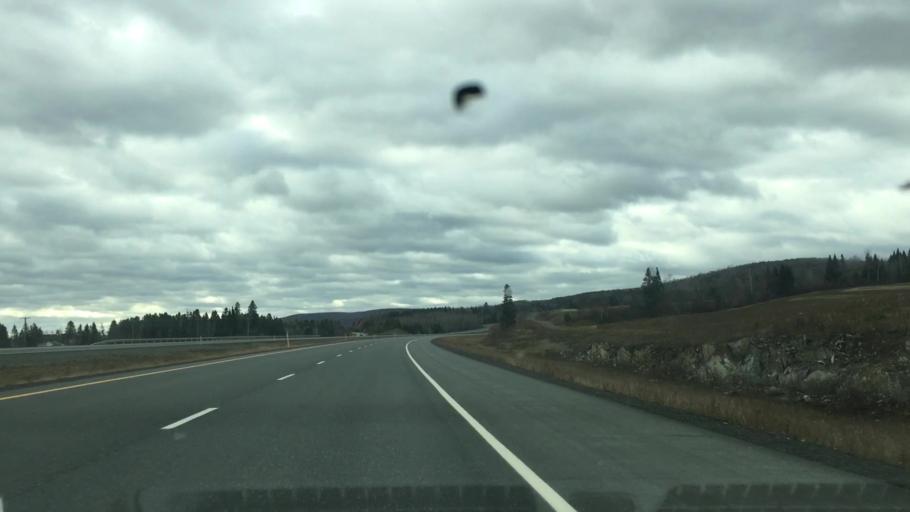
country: US
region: Maine
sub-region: Aroostook County
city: Fort Fairfield
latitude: 46.7381
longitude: -67.7171
